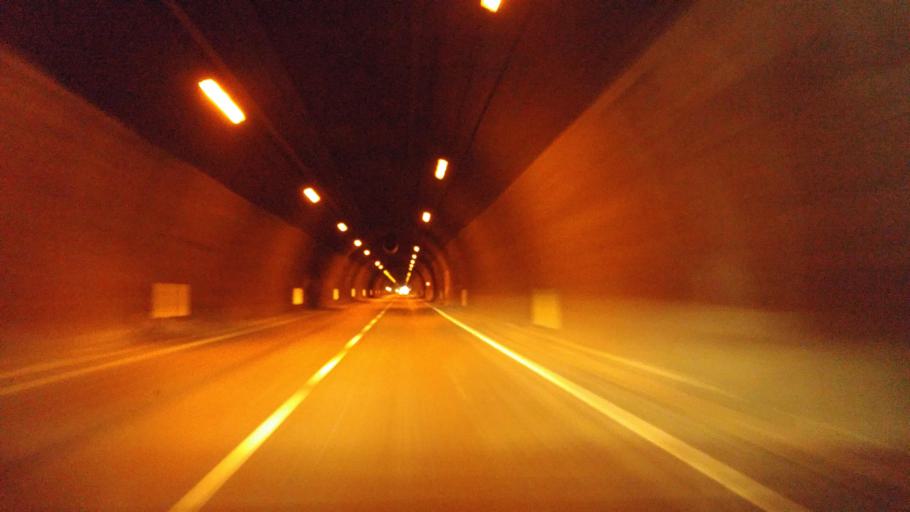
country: IT
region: The Marches
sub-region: Provincia di Pesaro e Urbino
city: Canavaccio
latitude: 43.6562
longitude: 12.7297
